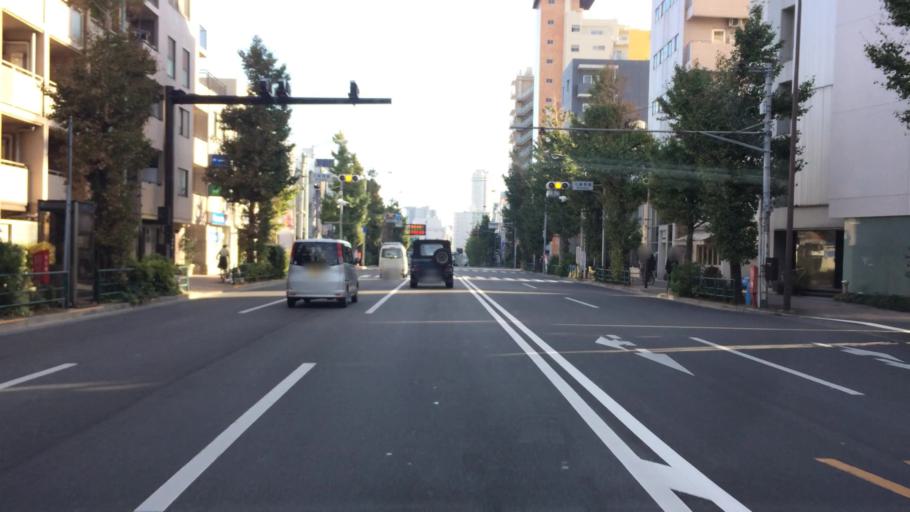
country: JP
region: Tokyo
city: Tokyo
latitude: 35.6309
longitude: 139.7023
